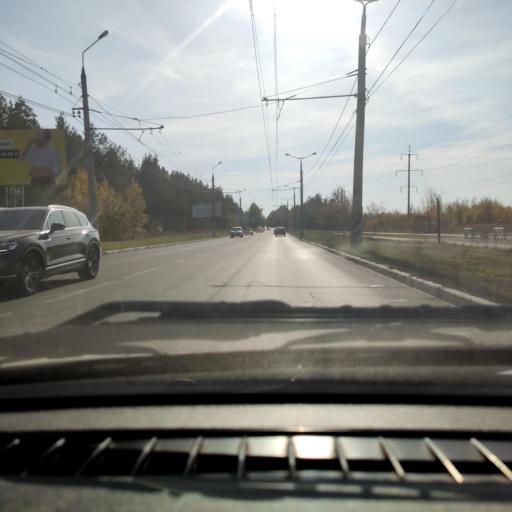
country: RU
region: Samara
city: Tol'yatti
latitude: 53.4973
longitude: 49.3880
